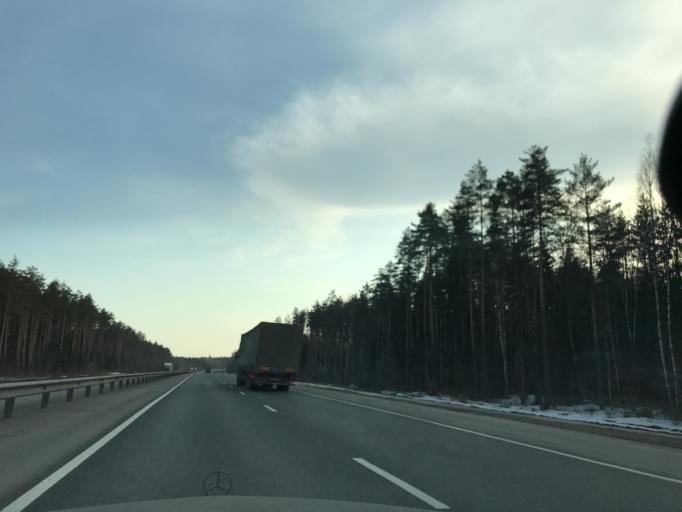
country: RU
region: Vladimir
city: Kameshkovo
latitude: 56.1853
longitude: 40.9489
